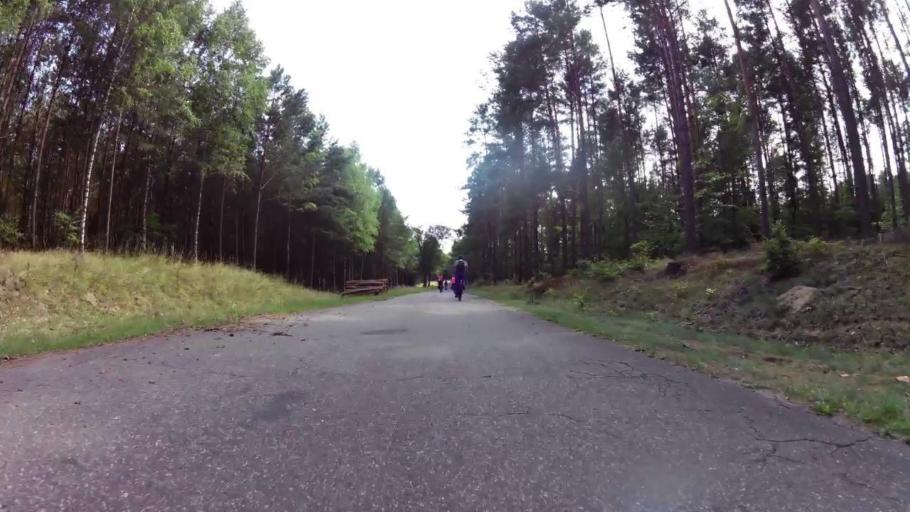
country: PL
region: West Pomeranian Voivodeship
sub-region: Powiat choszczenski
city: Drawno
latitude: 53.3461
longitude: 15.7041
